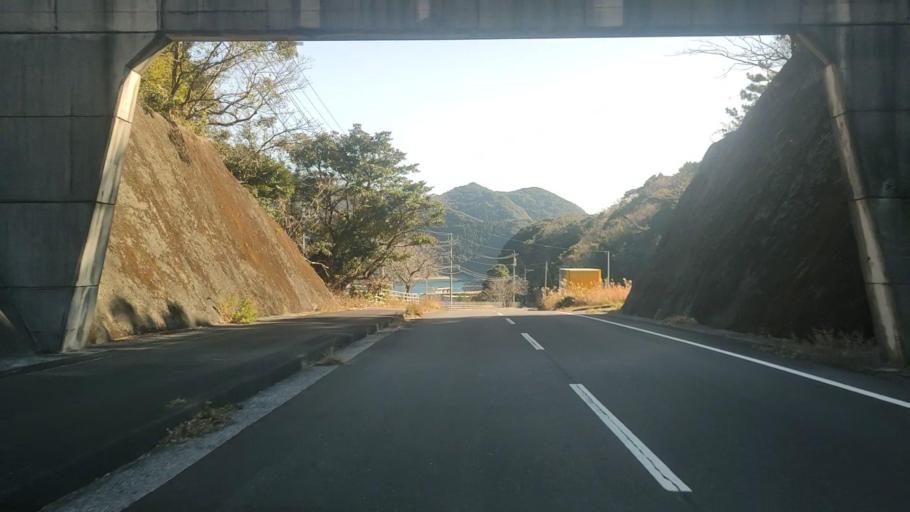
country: JP
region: Oita
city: Saiki
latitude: 32.7943
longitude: 131.9020
